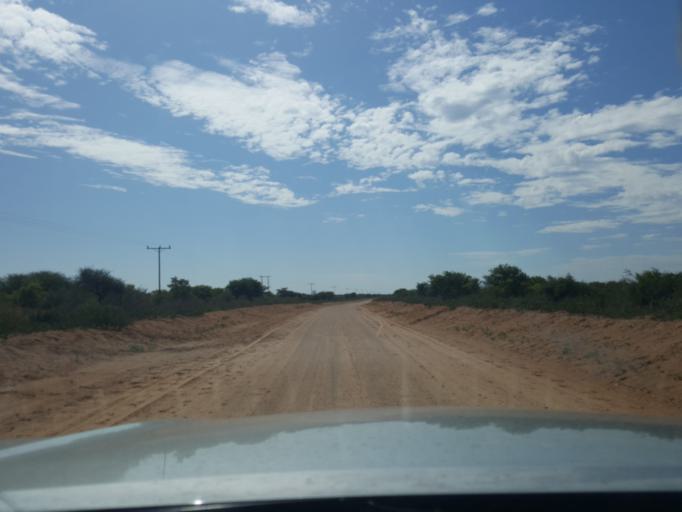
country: BW
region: Kweneng
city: Khudumelapye
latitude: -23.8605
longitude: 24.8840
